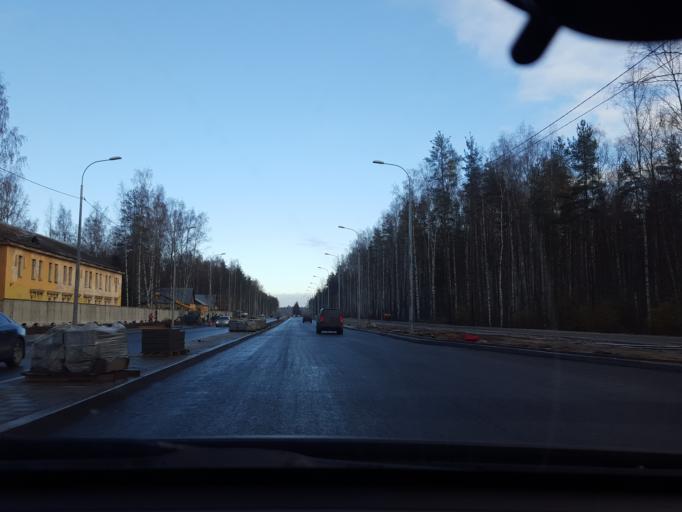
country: RU
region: St.-Petersburg
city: Pargolovo
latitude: 60.0579
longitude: 30.2420
